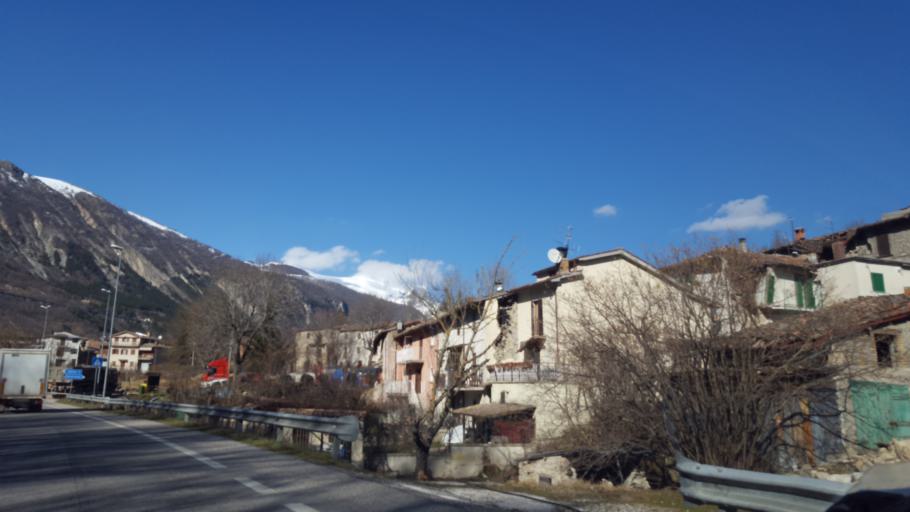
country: IT
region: Latium
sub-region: Provincia di Rieti
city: Accumoli
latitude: 42.7312
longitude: 13.2694
